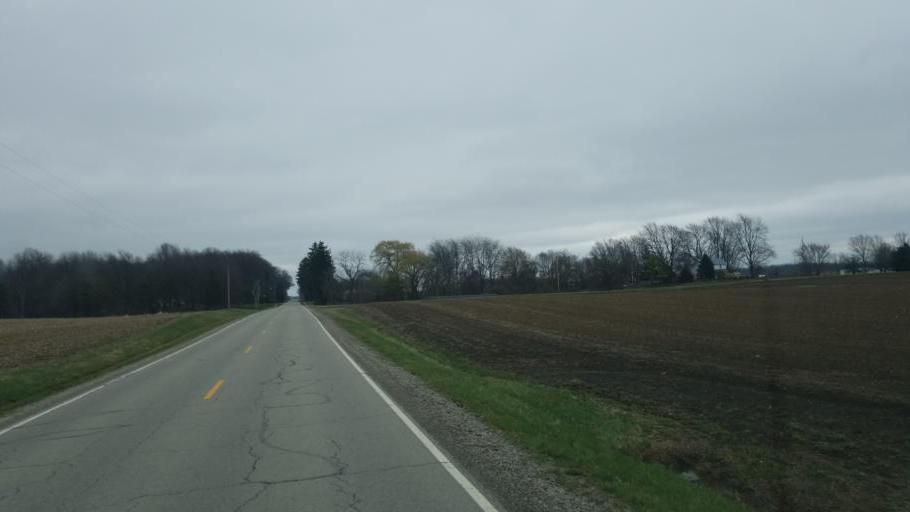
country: US
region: Ohio
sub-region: Crawford County
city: Bucyrus
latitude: 40.8193
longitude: -83.0532
